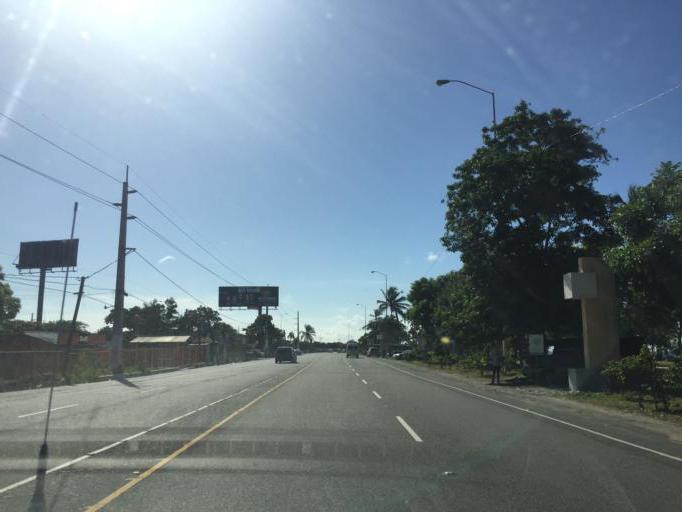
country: DO
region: Santo Domingo
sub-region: Santo Domingo
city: Boca Chica
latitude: 18.4476
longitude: -69.6818
